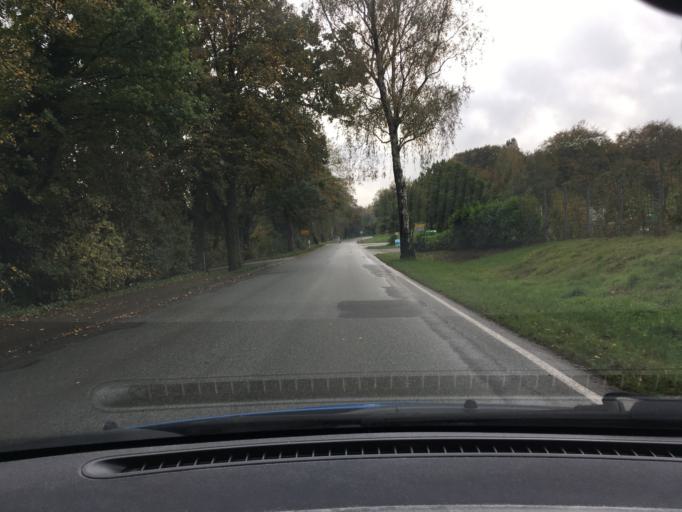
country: DE
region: Schleswig-Holstein
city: Tensfeld
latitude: 54.0417
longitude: 10.3181
